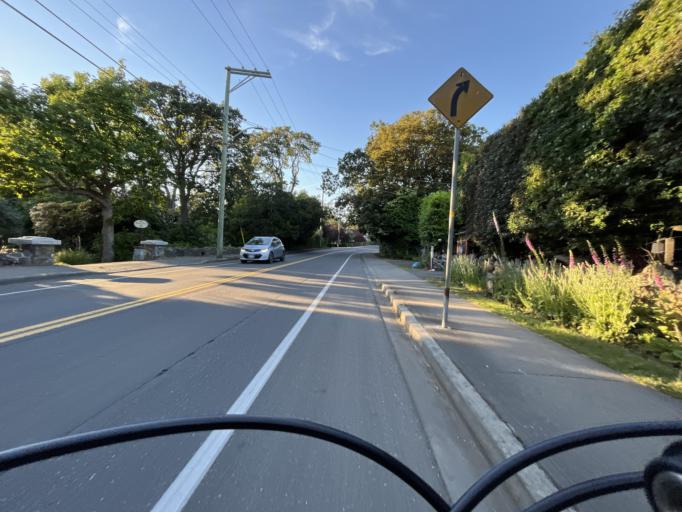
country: CA
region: British Columbia
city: Oak Bay
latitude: 48.4172
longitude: -123.3275
